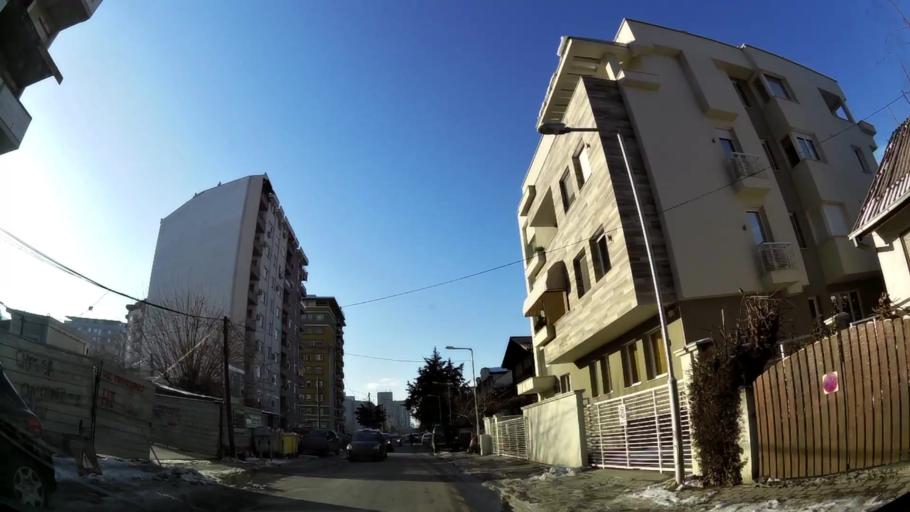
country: MK
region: Karpos
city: Skopje
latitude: 41.9987
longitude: 21.3965
